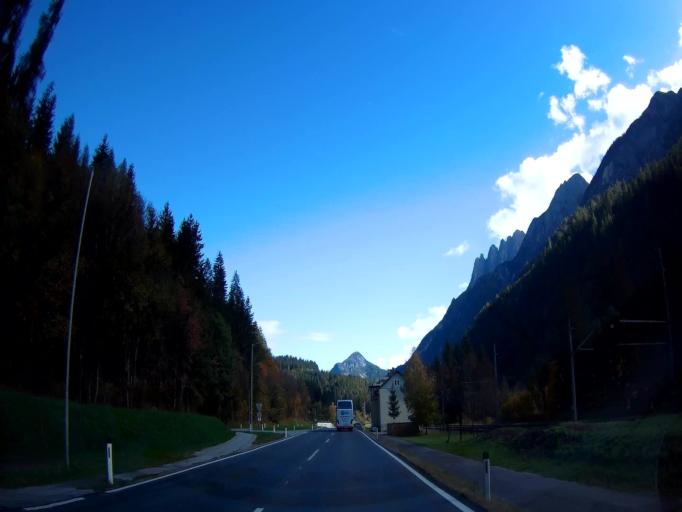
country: AT
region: Tyrol
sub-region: Politischer Bezirk Lienz
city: Leisach
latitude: 46.7847
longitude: 12.6726
